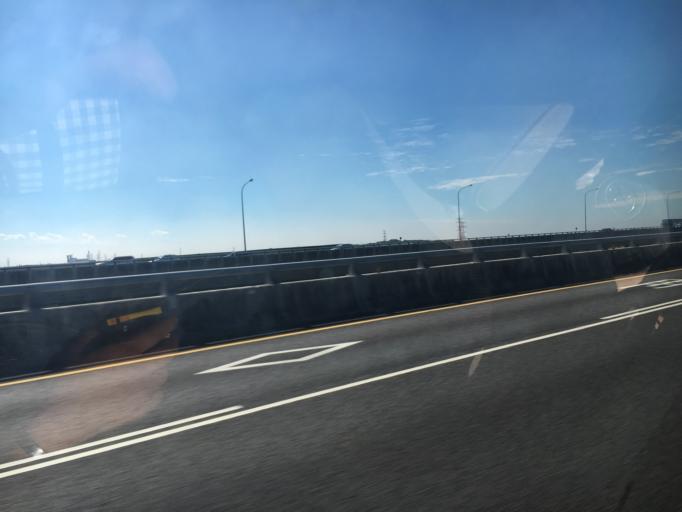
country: TW
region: Taiwan
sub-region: Taoyuan
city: Taoyuan
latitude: 25.0659
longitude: 121.3501
